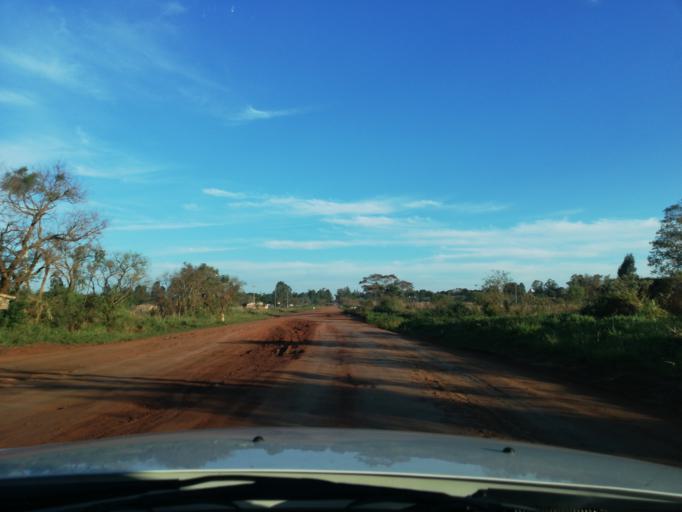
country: AR
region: Misiones
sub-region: Departamento de Capital
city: Posadas
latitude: -27.4686
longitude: -55.9708
